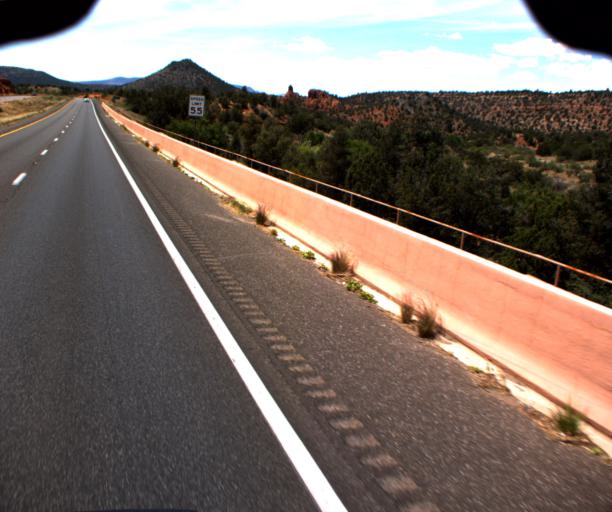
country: US
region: Arizona
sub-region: Yavapai County
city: West Sedona
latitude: 34.8449
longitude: -111.8513
